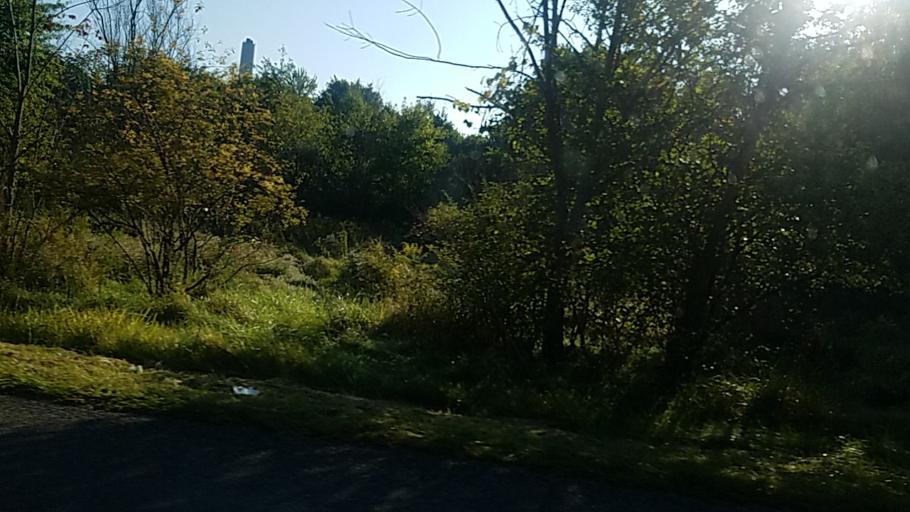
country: US
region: Ohio
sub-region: Trumbull County
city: Niles
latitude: 41.1647
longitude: -80.7535
